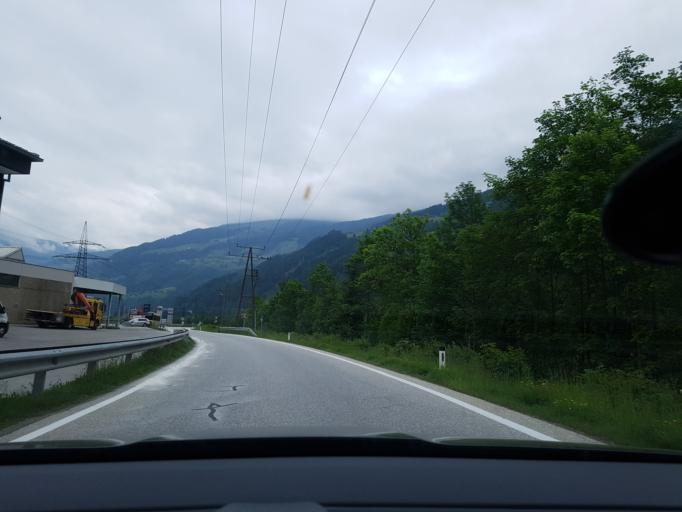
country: AT
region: Tyrol
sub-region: Politischer Bezirk Schwaz
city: Zell am Ziller
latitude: 47.2286
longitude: 11.8928
